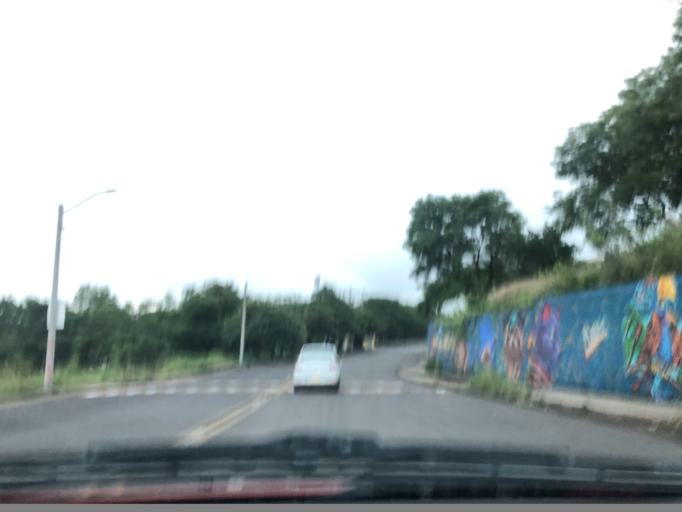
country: MX
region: Jalisco
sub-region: Tlajomulco de Zuniga
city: Altus Bosques
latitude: 20.6143
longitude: -103.3871
